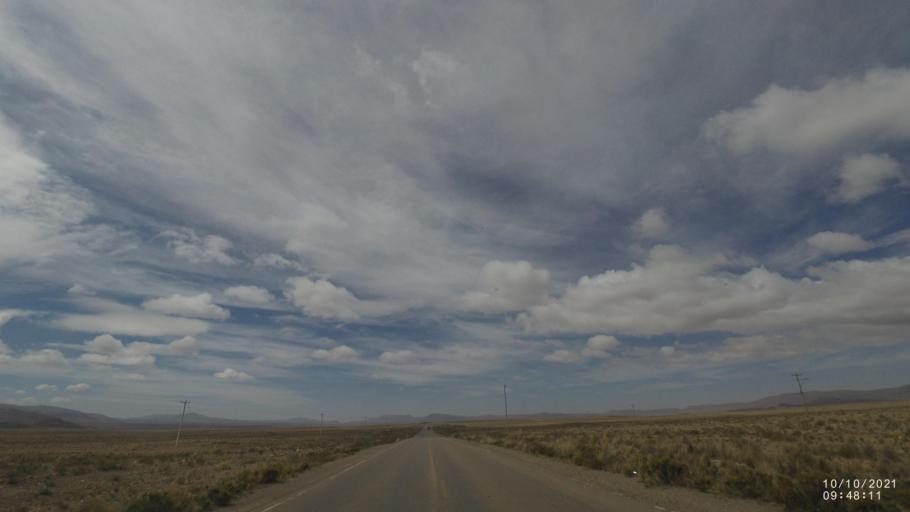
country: BO
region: La Paz
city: Quime
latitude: -17.2055
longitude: -67.3422
